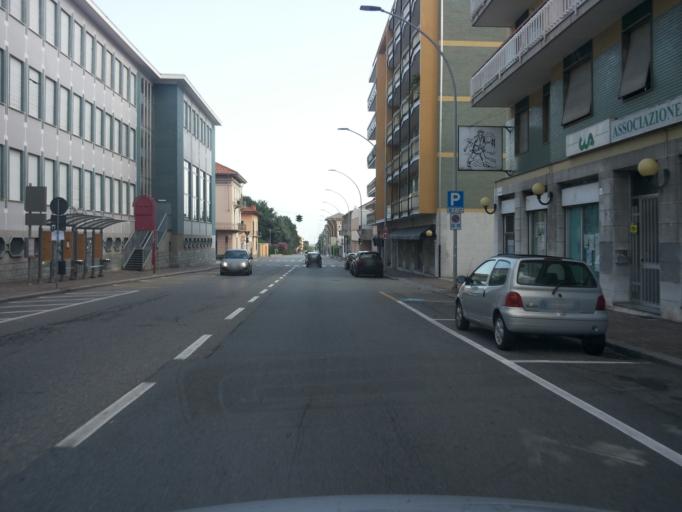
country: IT
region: Piedmont
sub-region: Provincia di Biella
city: Biella
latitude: 45.5592
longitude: 8.0526
